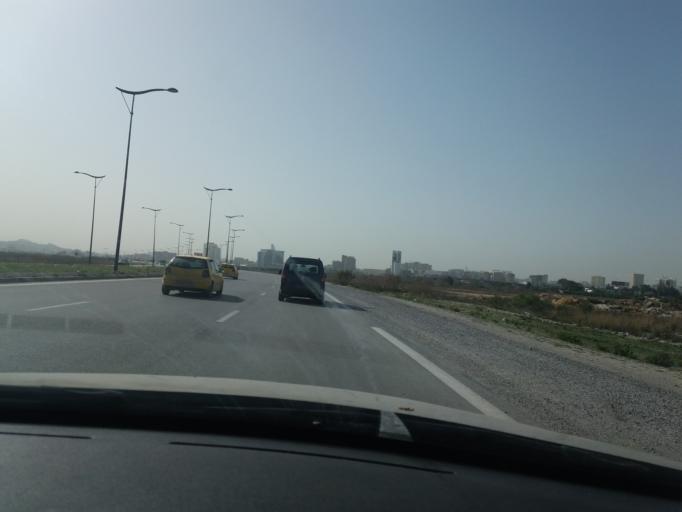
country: TN
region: Tunis
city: Tunis
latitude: 36.8182
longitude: 10.1971
